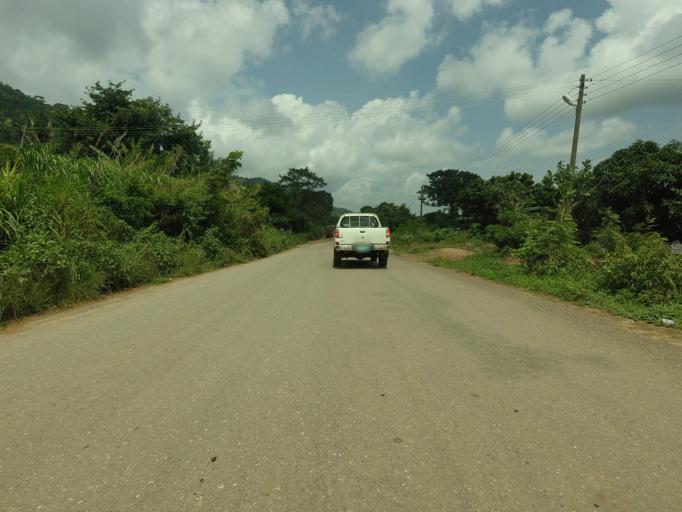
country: GH
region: Volta
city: Ho
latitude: 6.7321
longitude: 0.3467
